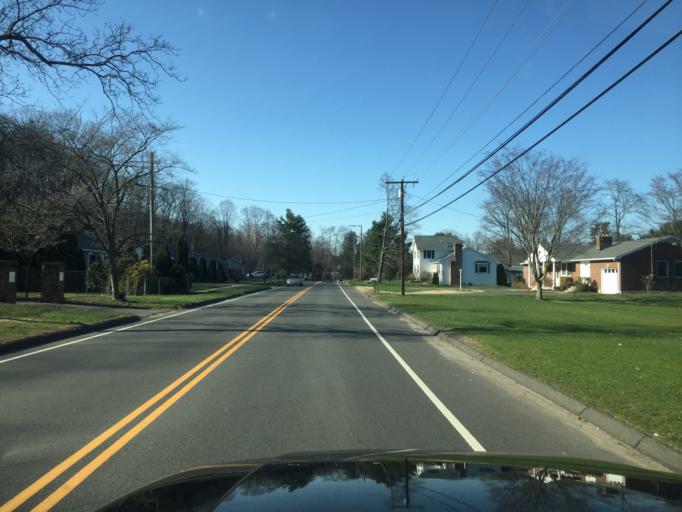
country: US
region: Connecticut
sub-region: Hartford County
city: Bristol
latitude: 41.6486
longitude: -72.9238
